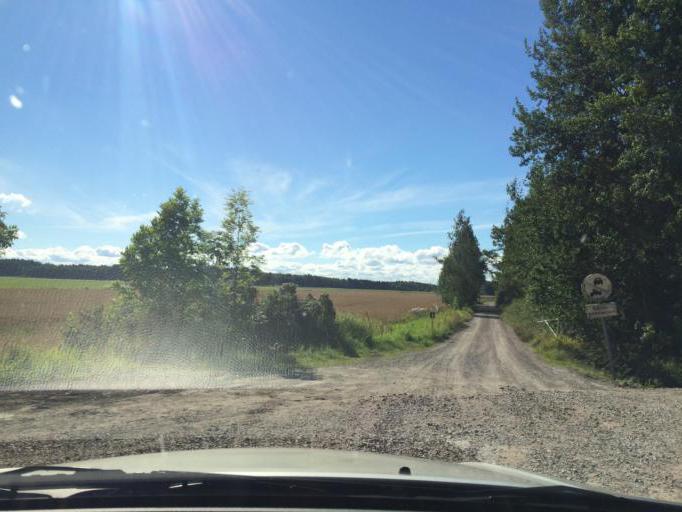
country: SE
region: Vaestmanland
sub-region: Vasteras
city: Vasteras
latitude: 59.5809
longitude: 16.4936
